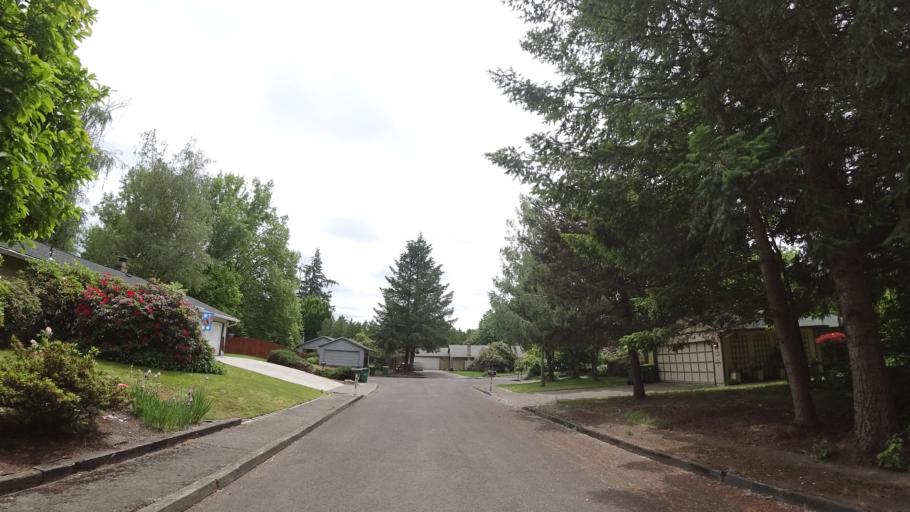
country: US
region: Oregon
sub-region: Washington County
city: Garden Home-Whitford
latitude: 45.4566
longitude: -122.7583
